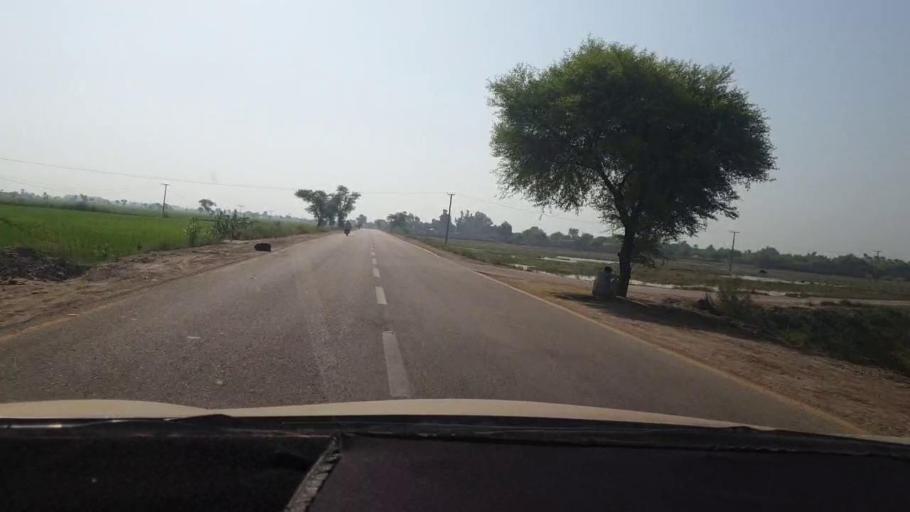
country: PK
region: Sindh
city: Miro Khan
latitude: 27.7256
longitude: 68.1368
